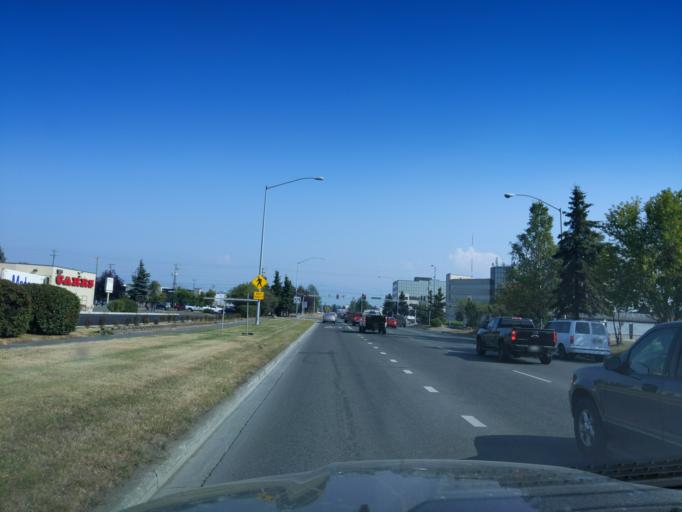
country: US
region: Alaska
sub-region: Anchorage Municipality
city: Anchorage
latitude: 61.1937
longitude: -149.9155
